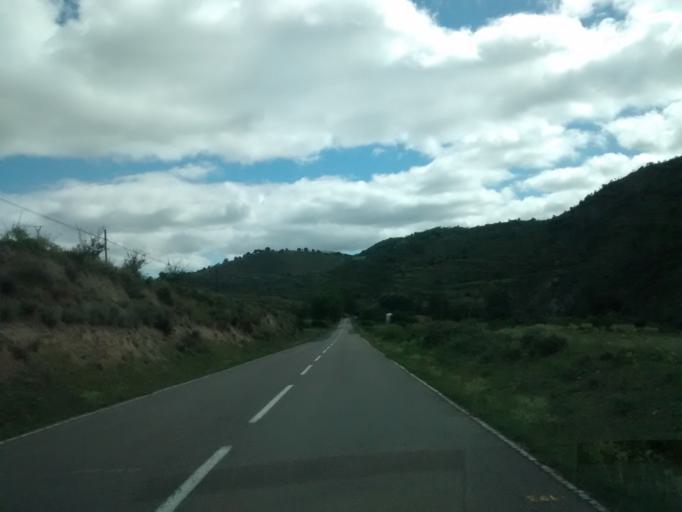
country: ES
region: La Rioja
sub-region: Provincia de La Rioja
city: Terroba
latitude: 42.2454
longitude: -2.4583
